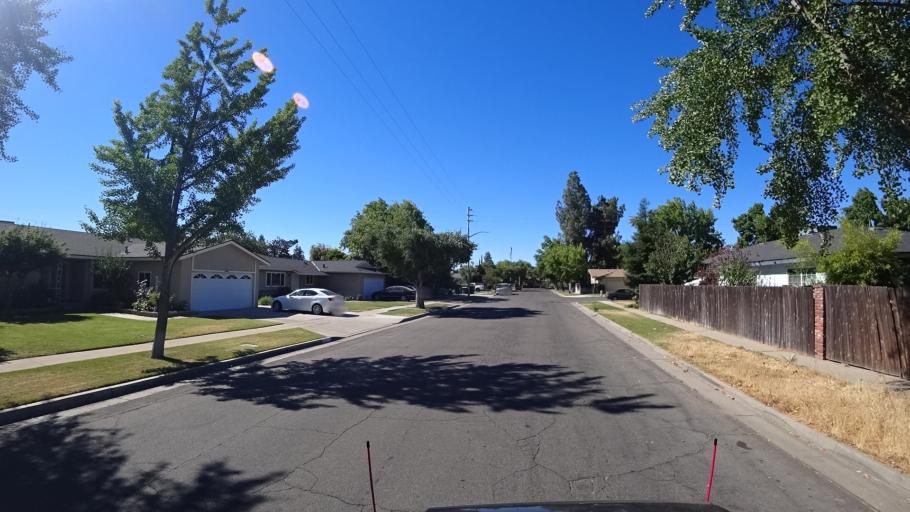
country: US
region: California
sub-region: Fresno County
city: Fresno
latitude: 36.7984
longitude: -119.8276
